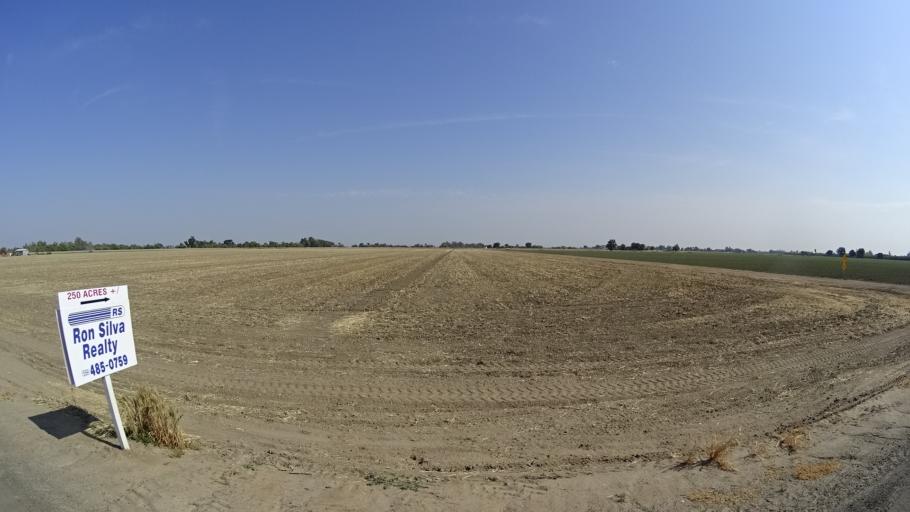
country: US
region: California
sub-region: Kings County
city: Lemoore Station
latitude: 36.3274
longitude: -119.8691
